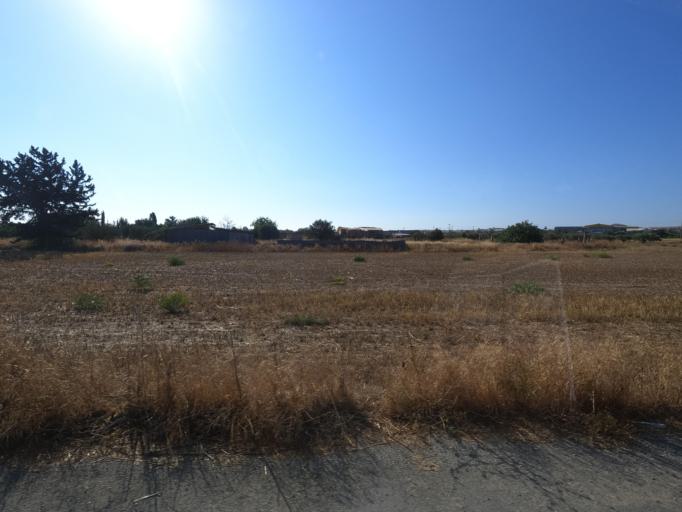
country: CY
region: Larnaka
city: Athienou
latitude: 35.0624
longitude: 33.5189
